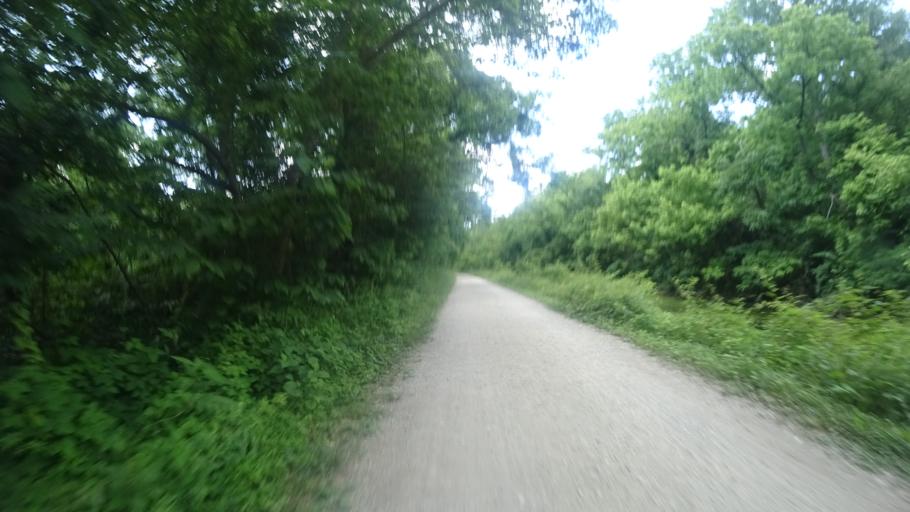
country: US
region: Maryland
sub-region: Montgomery County
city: Brookmont
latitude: 38.9457
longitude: -77.1244
